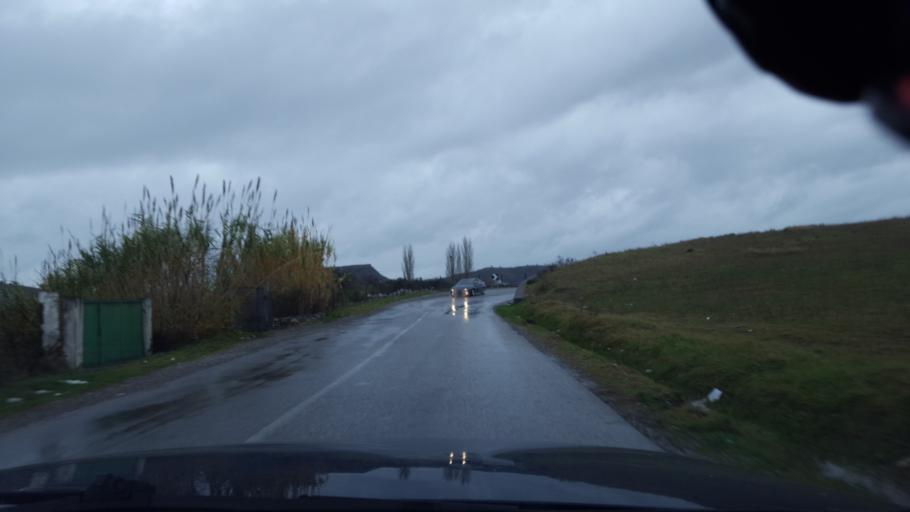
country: AL
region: Shkoder
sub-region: Rrethi i Shkodres
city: Berdica e Madhe
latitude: 42.0295
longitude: 19.4947
